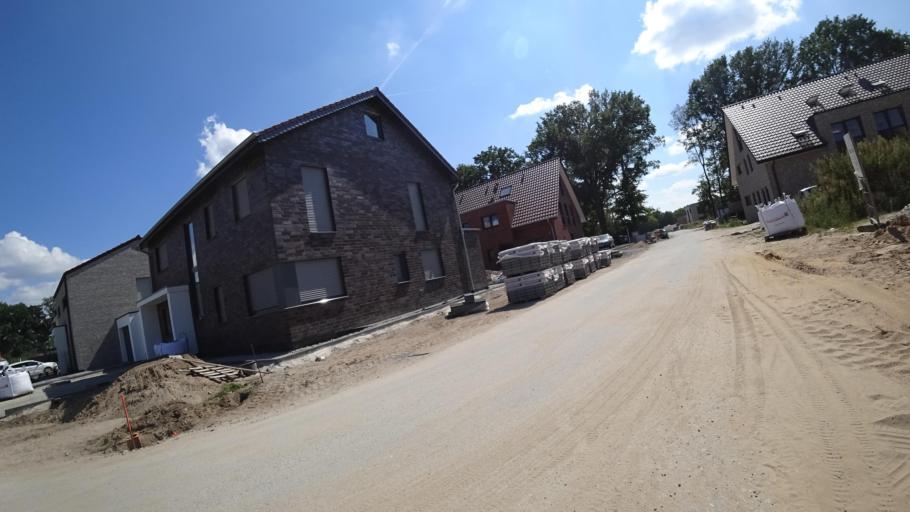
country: DE
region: North Rhine-Westphalia
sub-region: Regierungsbezirk Detmold
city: Guetersloh
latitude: 51.9312
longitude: 8.3904
